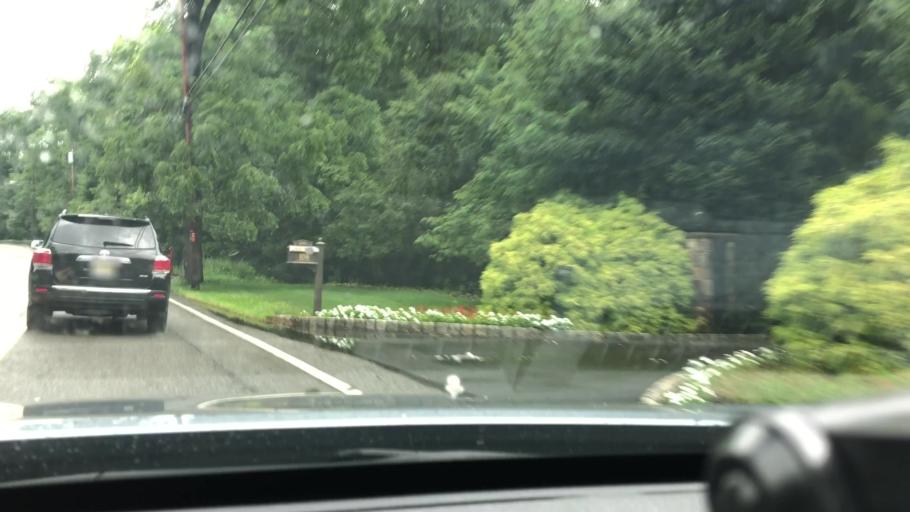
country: US
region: New Jersey
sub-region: Bergen County
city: Saddle River
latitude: 41.0256
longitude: -74.1023
